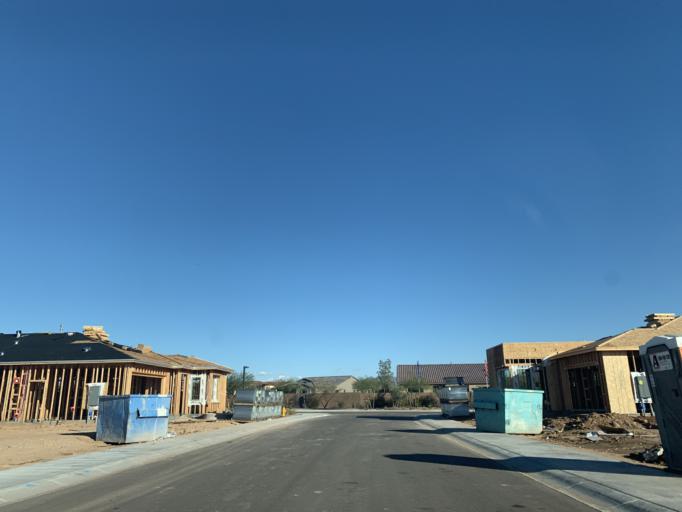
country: US
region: Arizona
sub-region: Maricopa County
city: Cave Creek
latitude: 33.6902
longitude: -112.0209
